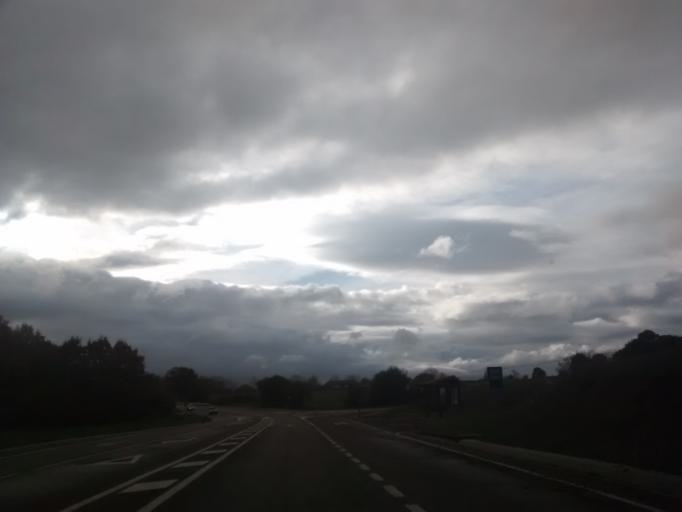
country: ES
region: Cantabria
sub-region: Provincia de Cantabria
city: San Miguel de Aguayo
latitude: 43.0086
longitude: -4.0541
